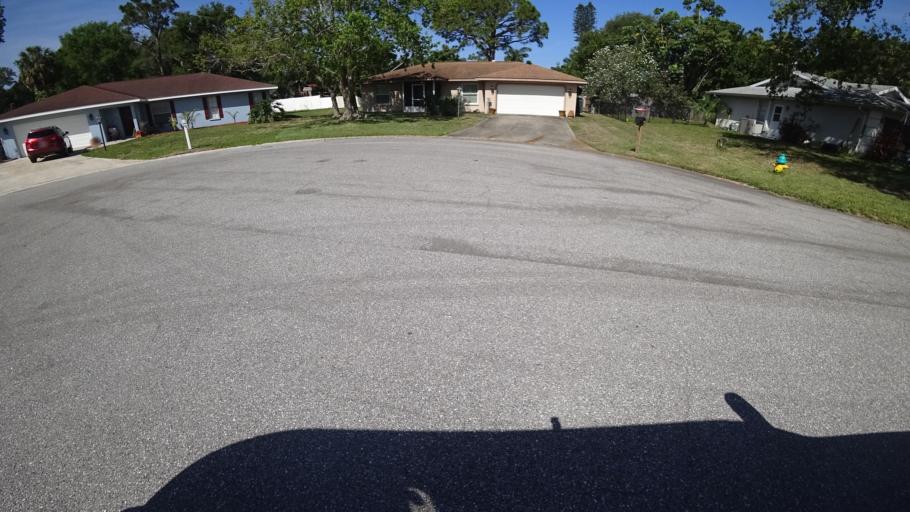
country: US
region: Florida
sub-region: Manatee County
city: West Bradenton
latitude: 27.5111
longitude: -82.6333
